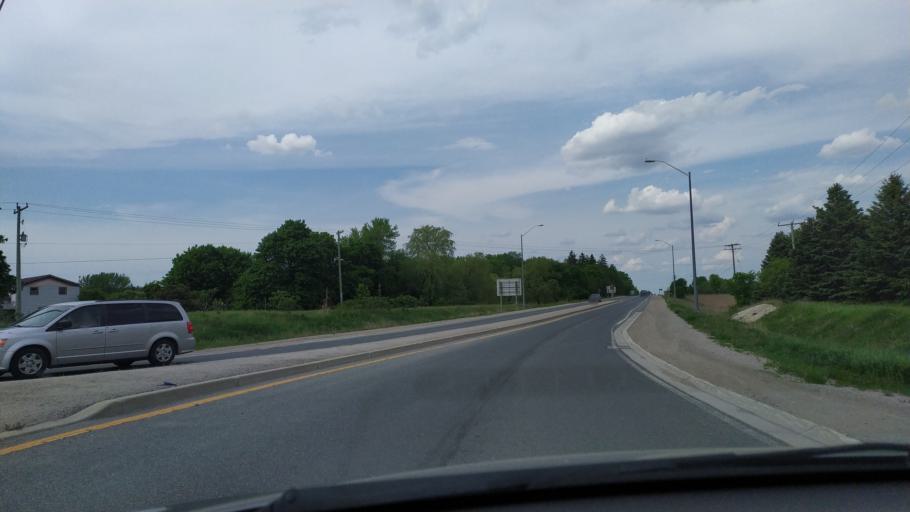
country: CA
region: Ontario
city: Stratford
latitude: 43.2704
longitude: -81.0677
